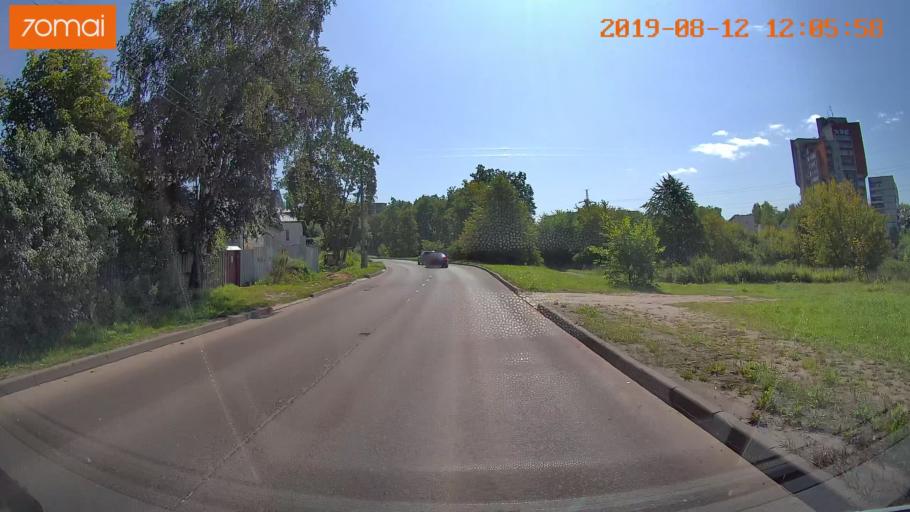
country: RU
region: Ivanovo
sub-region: Gorod Ivanovo
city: Ivanovo
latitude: 56.9906
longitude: 41.0193
